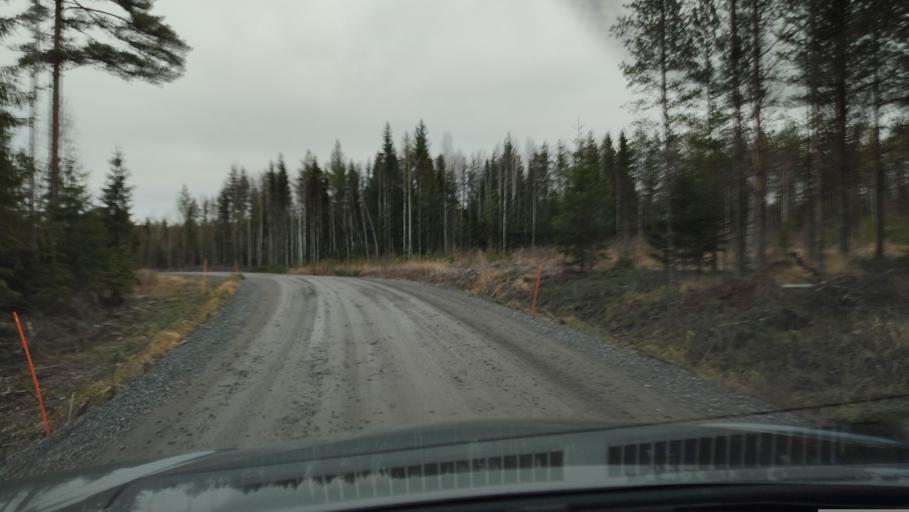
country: FI
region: Southern Ostrobothnia
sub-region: Suupohja
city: Karijoki
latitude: 62.1986
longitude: 21.5748
